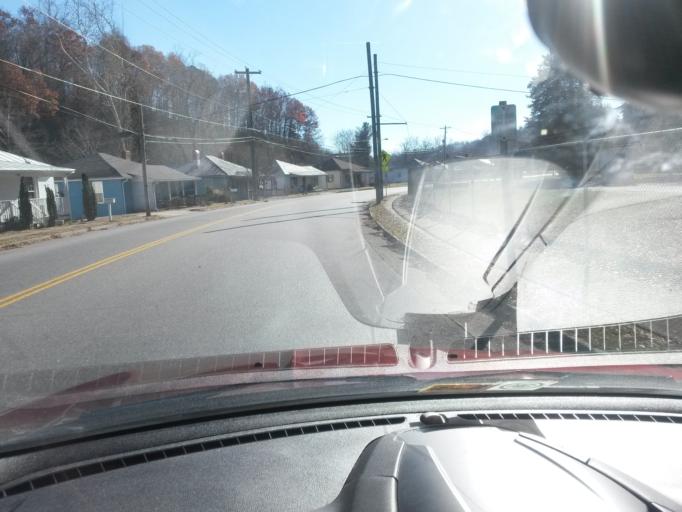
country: US
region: Virginia
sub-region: Henry County
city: Bassett
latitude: 36.7650
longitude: -79.9968
